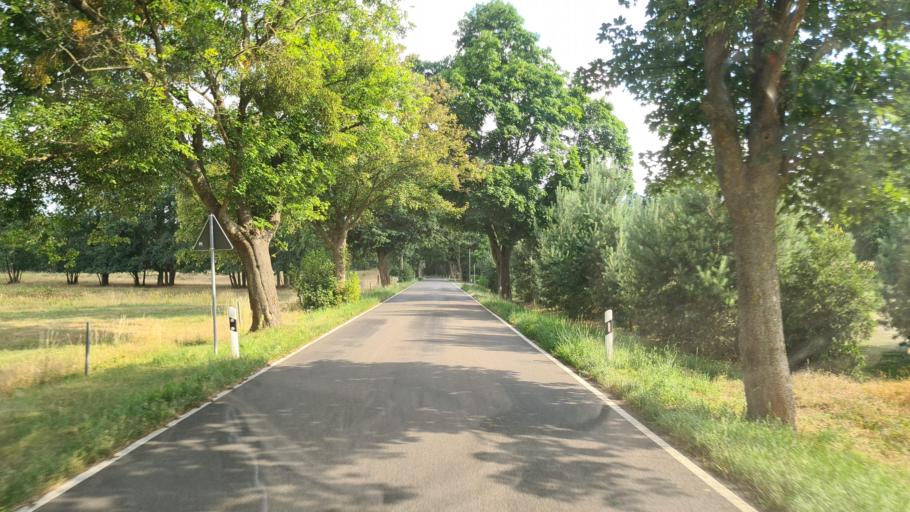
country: DE
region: Saxony-Anhalt
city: Kropstadt
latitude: 51.9375
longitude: 12.7090
